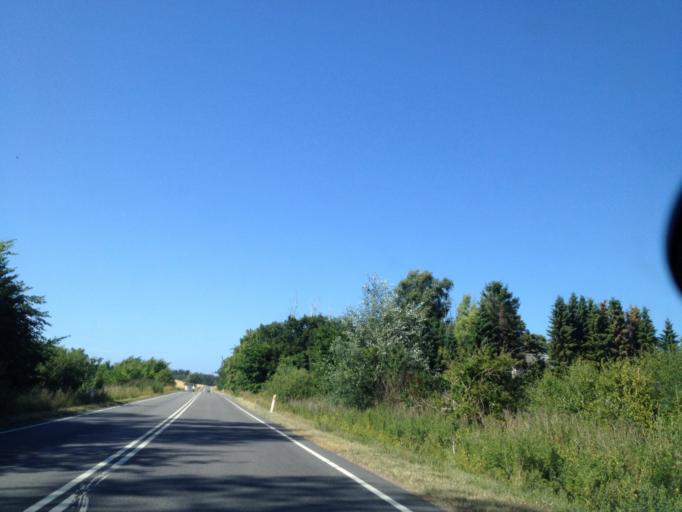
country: DK
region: Capital Region
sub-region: Gribskov Kommune
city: Graested
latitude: 56.0721
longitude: 12.3458
